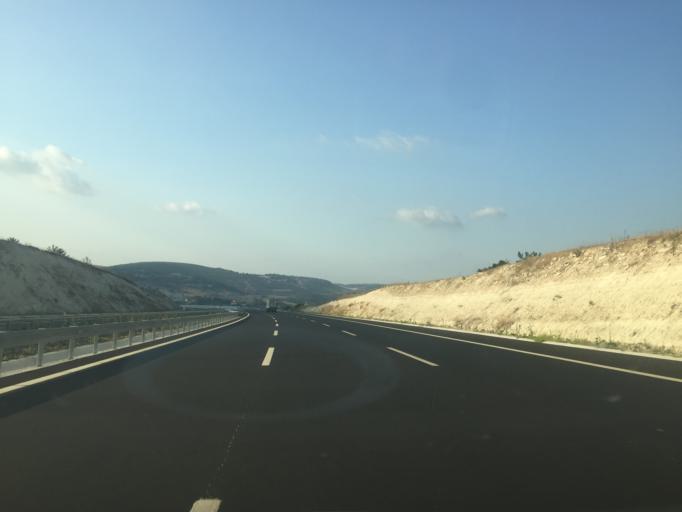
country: TR
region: Balikesir
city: Ertugrul
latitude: 39.5673
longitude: 27.7025
